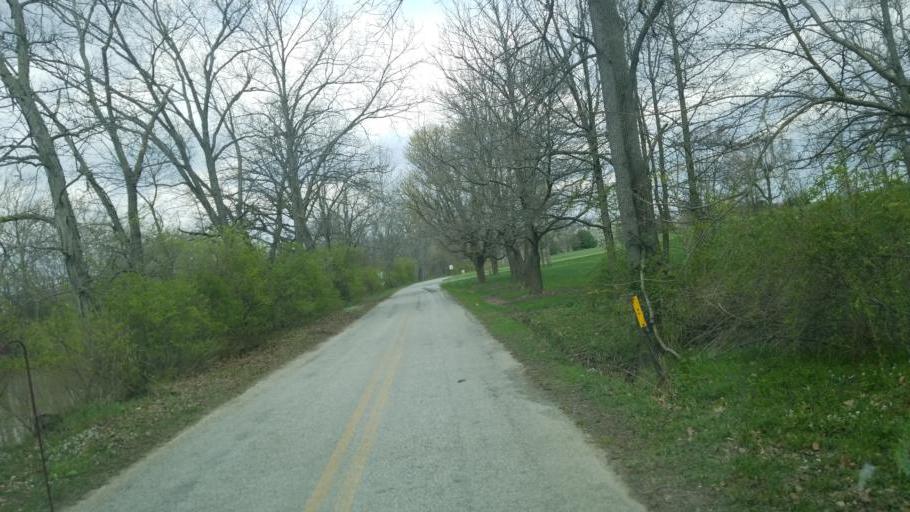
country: US
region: Ohio
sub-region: Delaware County
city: Delaware
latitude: 40.3299
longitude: -83.1720
